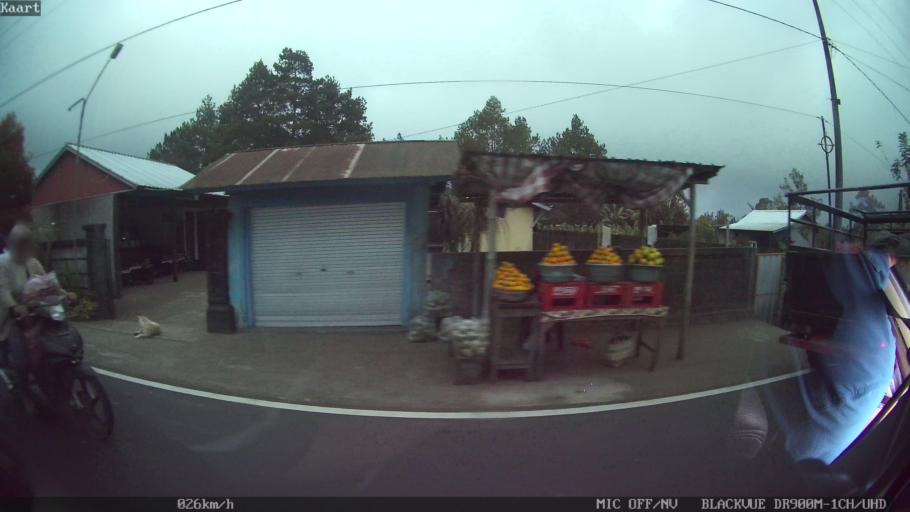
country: ID
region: Bali
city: Banjar Kedisan
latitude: -8.2728
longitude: 115.3300
